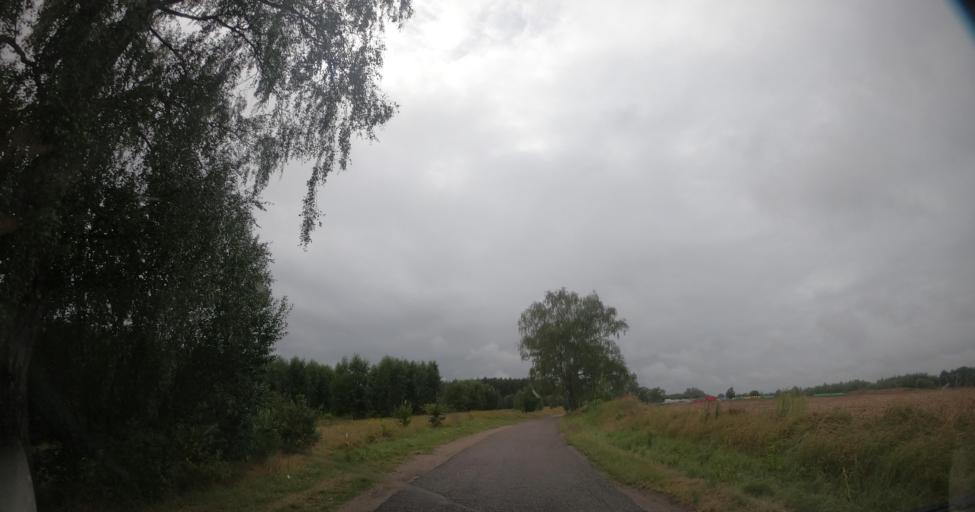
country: PL
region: West Pomeranian Voivodeship
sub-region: Powiat lobeski
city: Wegorzyno
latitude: 53.5388
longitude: 15.5470
